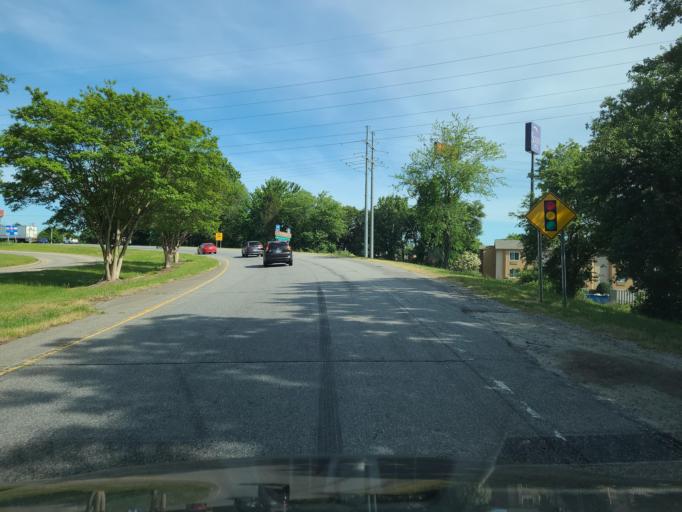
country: US
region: North Carolina
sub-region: Catawba County
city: Hickory
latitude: 35.7126
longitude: -81.3146
